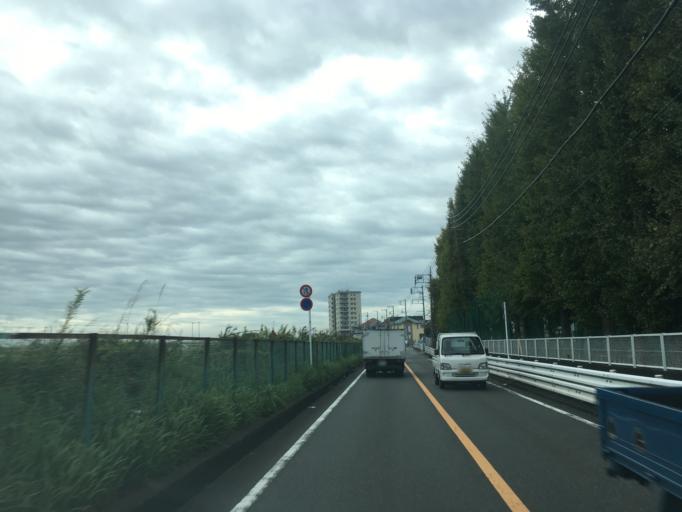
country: JP
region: Tokyo
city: Chofugaoka
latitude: 35.6449
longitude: 139.5209
